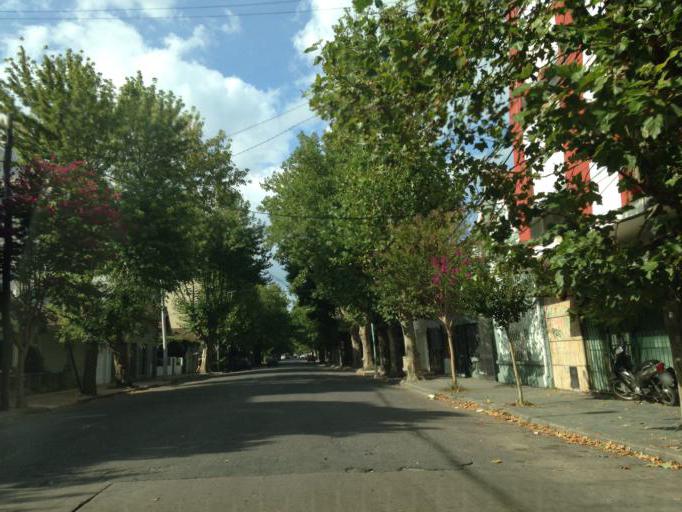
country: AR
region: Buenos Aires
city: Mar del Plata
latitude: -37.9913
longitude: -57.5518
